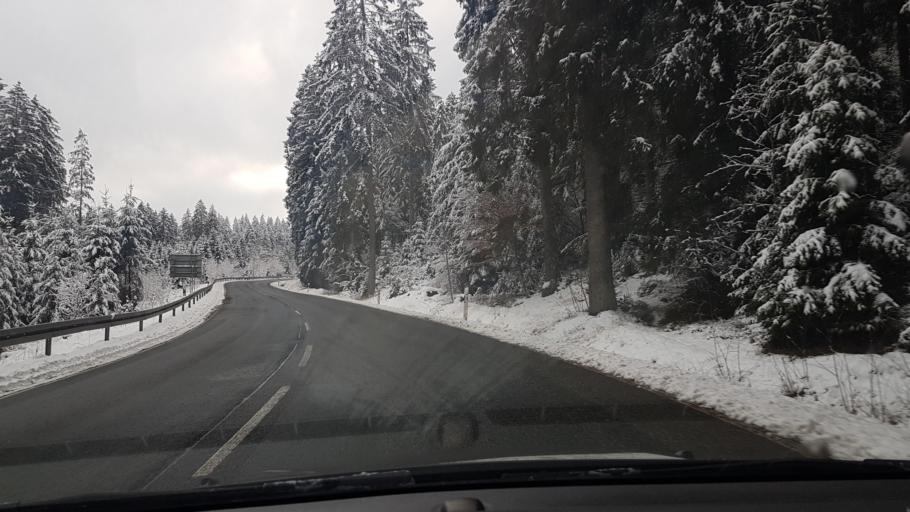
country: DE
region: Lower Saxony
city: Wildemann
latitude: 51.8136
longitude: 10.2768
